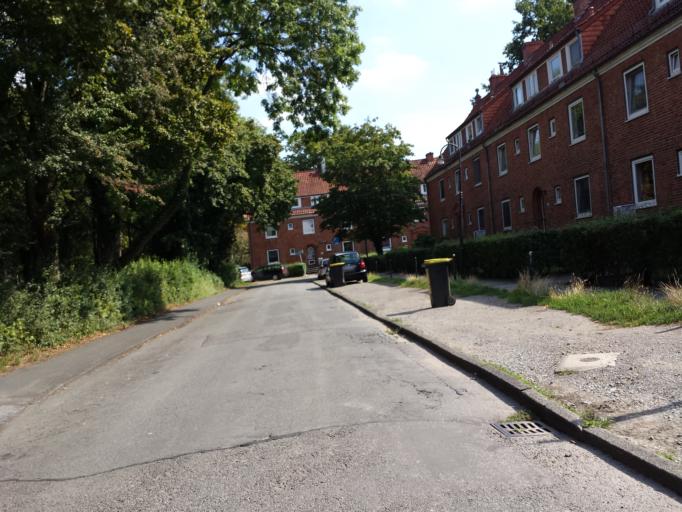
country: DE
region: Bremen
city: Bremen
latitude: 53.0427
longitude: 8.8179
